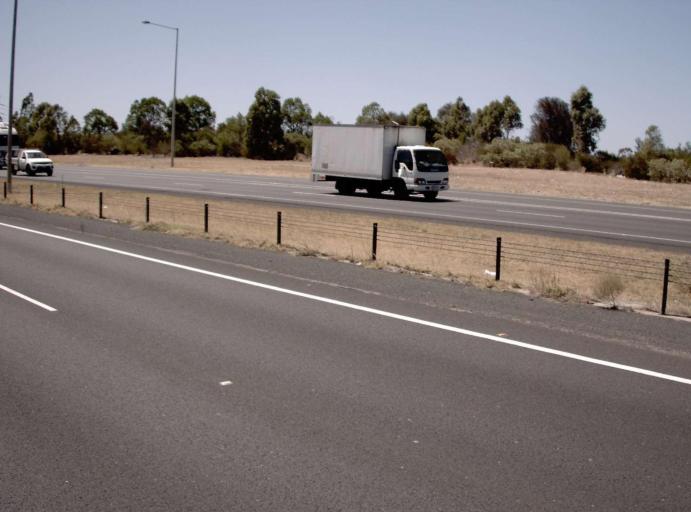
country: AU
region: Victoria
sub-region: Brimbank
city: Kealba
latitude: -37.7418
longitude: 144.8472
